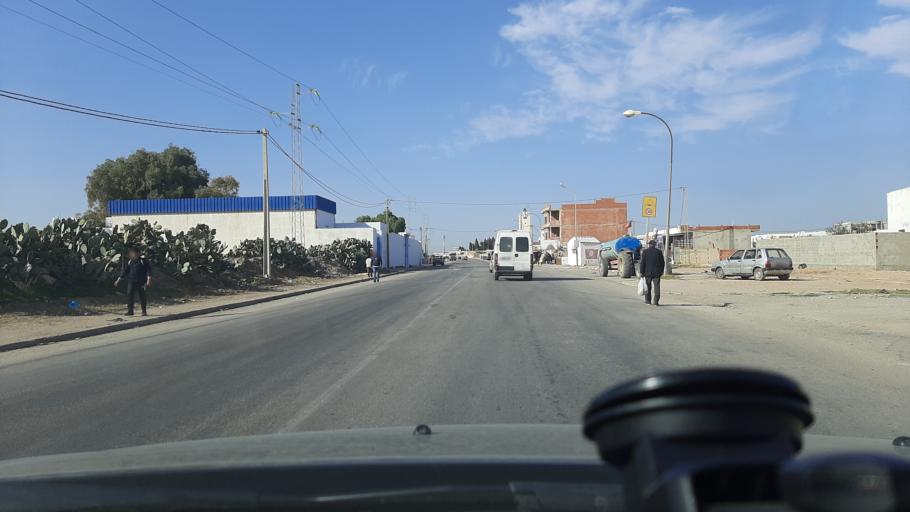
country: TN
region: Safaqis
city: Sfax
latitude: 34.7895
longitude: 10.6497
